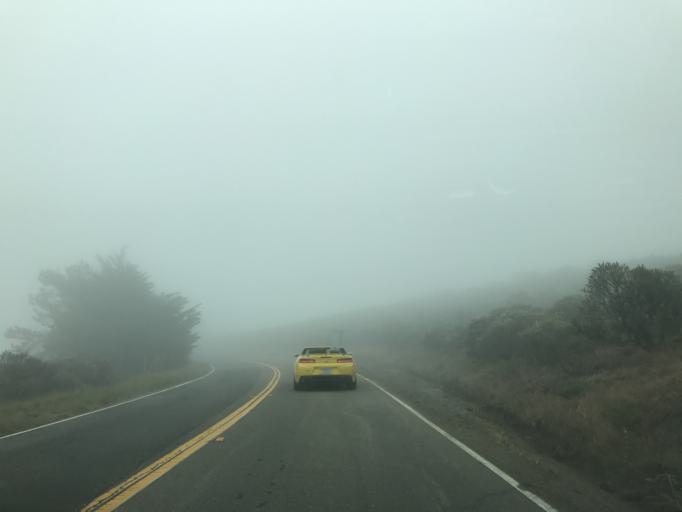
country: US
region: California
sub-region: Sonoma County
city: Monte Rio
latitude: 38.4779
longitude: -123.1593
